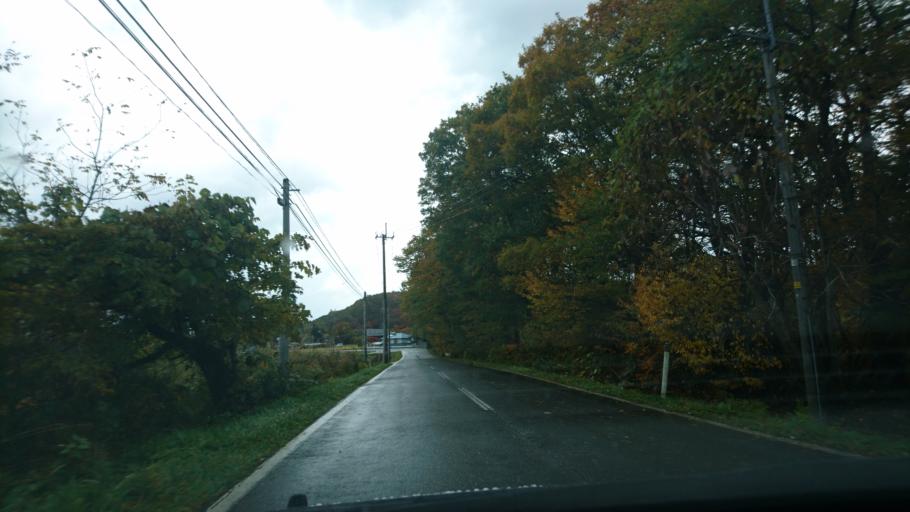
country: JP
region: Iwate
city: Shizukuishi
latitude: 39.6205
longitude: 140.9466
